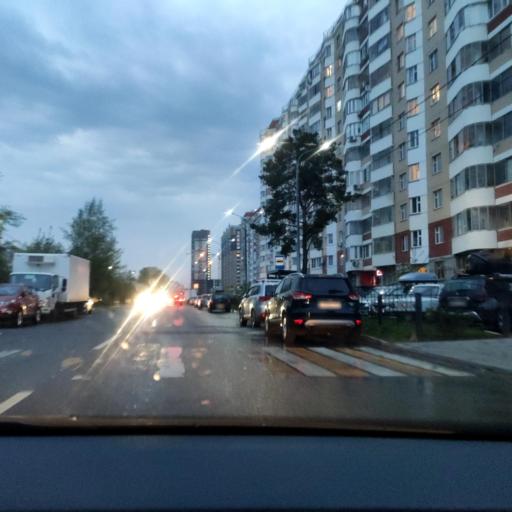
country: RU
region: Moskovskaya
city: Korolev
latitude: 55.9084
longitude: 37.8265
